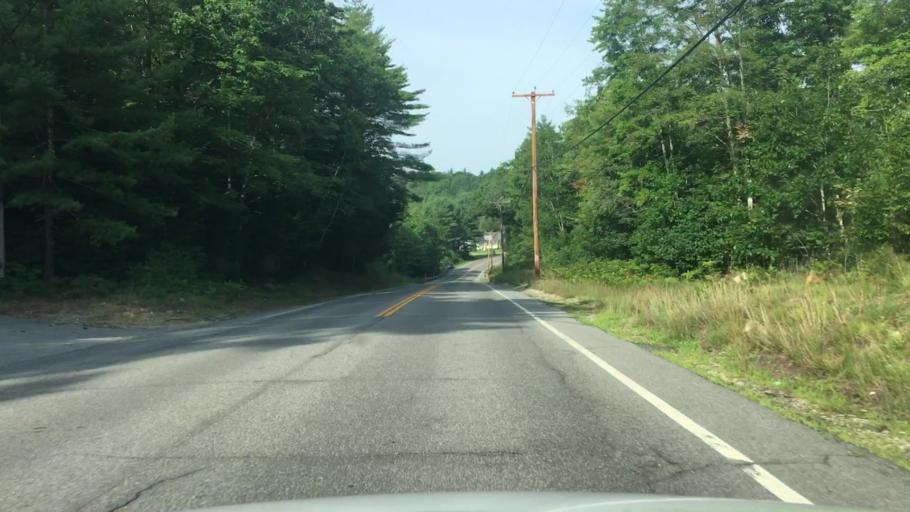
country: US
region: Maine
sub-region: York County
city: Cornish
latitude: 43.8040
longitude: -70.8502
